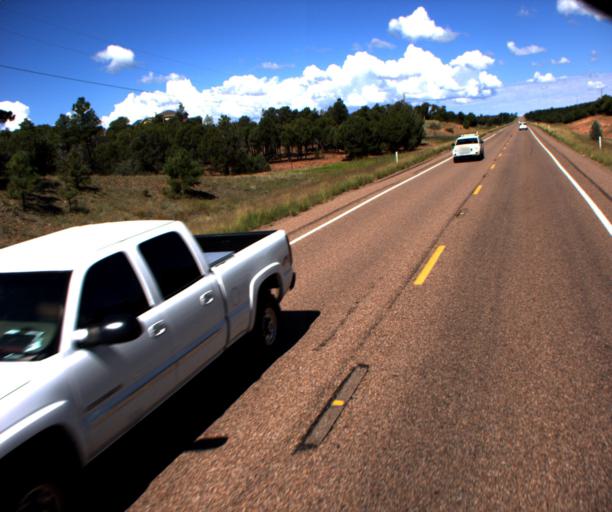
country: US
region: Arizona
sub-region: Navajo County
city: Linden
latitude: 34.3220
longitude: -110.2530
